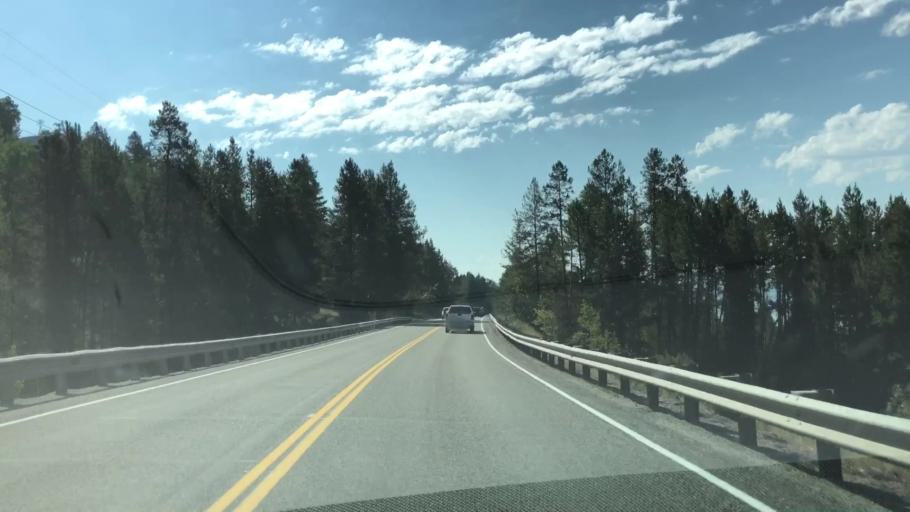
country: US
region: Idaho
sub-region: Teton County
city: Victor
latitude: 43.3065
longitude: -111.1356
